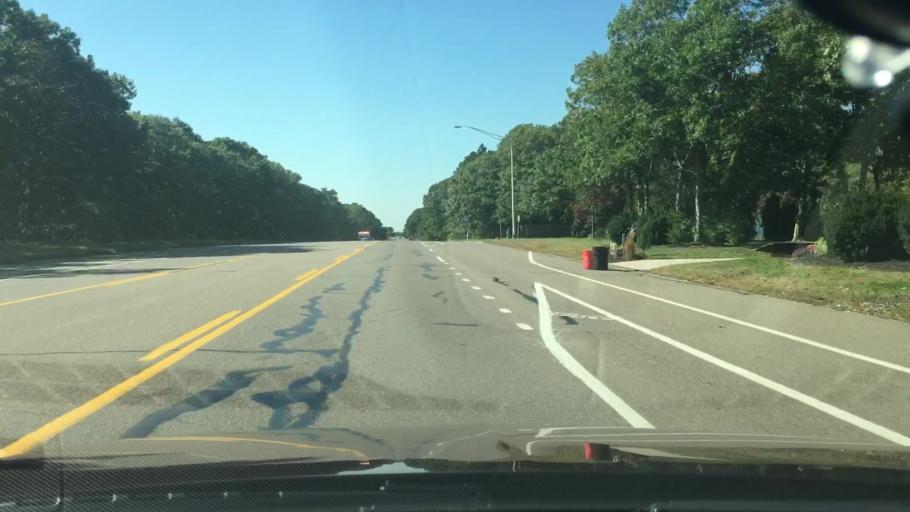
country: US
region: New York
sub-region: Suffolk County
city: North Patchogue
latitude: 40.7959
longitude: -72.9827
